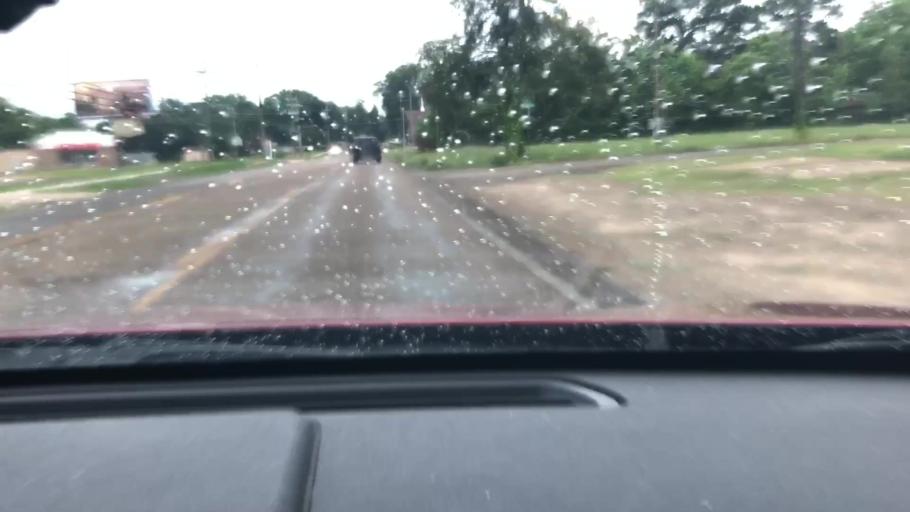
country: US
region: Texas
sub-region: Bowie County
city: Nash
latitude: 33.4425
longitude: -94.1248
